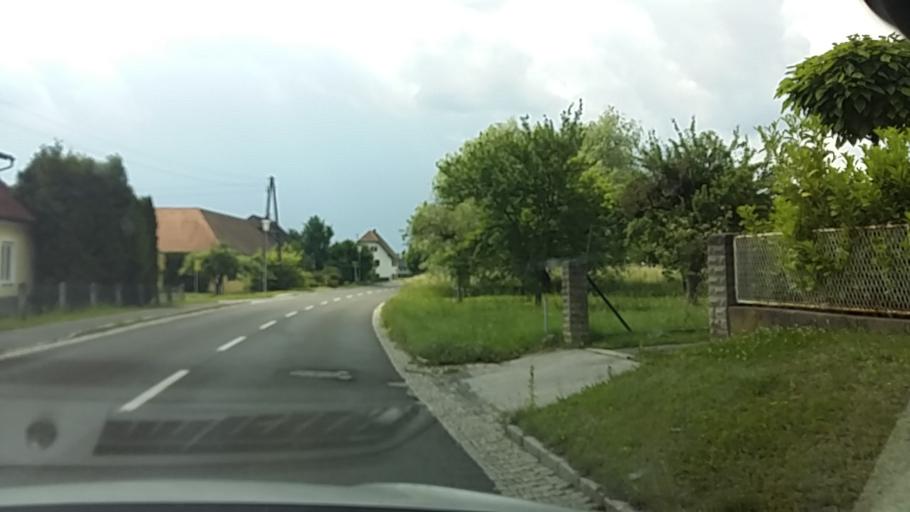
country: AT
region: Styria
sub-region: Politischer Bezirk Hartberg-Fuerstenfeld
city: Soechau
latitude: 47.0326
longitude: 16.0123
